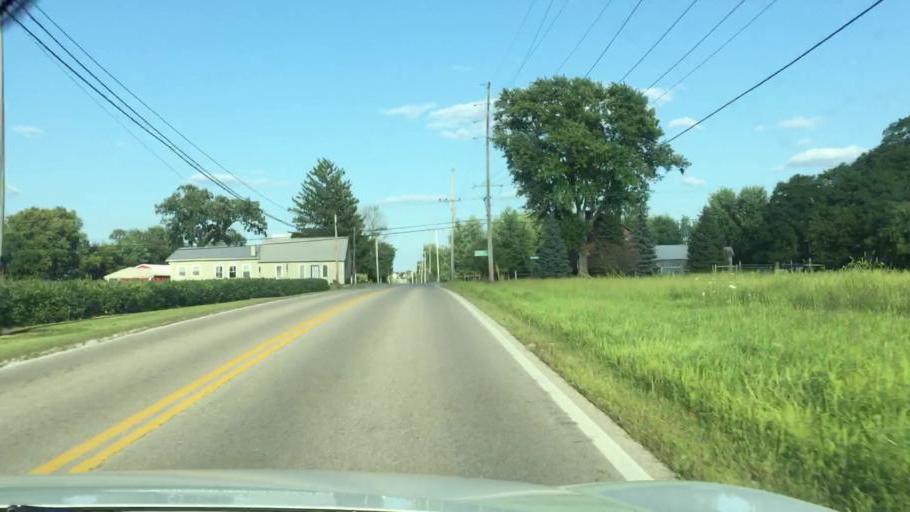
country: US
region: Ohio
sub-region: Clark County
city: Northridge
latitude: 39.9391
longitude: -83.7117
